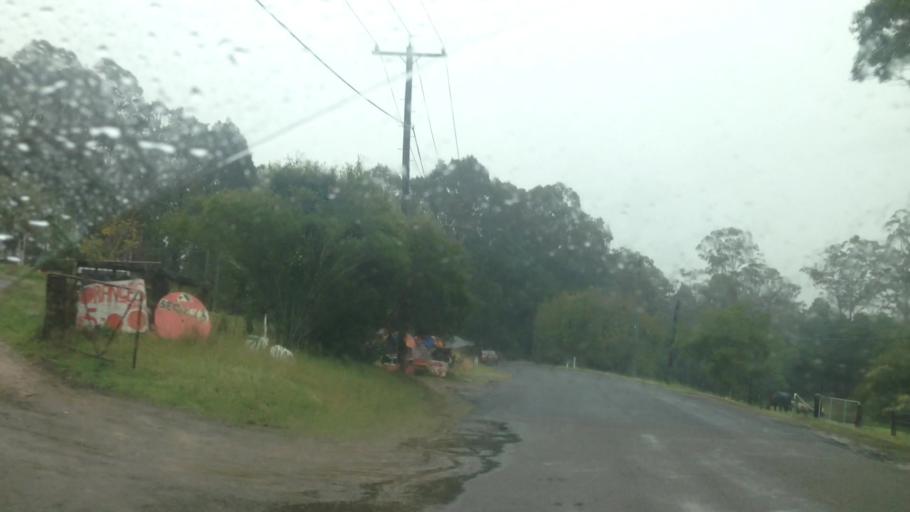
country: AU
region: New South Wales
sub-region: Wyong Shire
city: Little Jilliby
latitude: -33.2080
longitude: 151.3685
